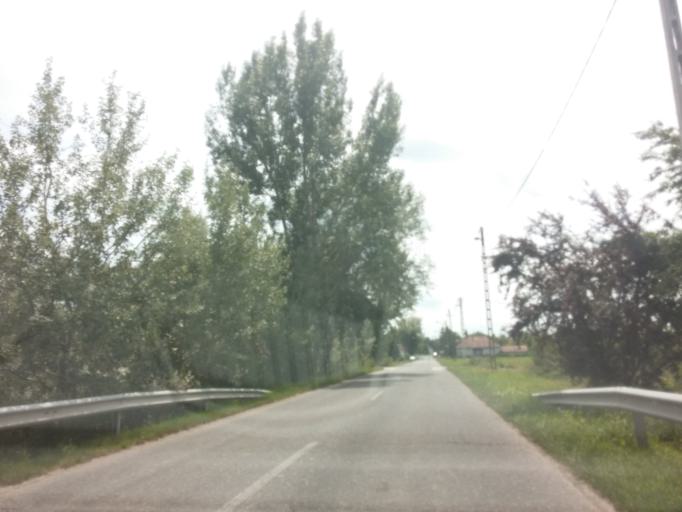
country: HU
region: Pest
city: Szigetcsep
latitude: 47.2739
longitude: 18.9758
